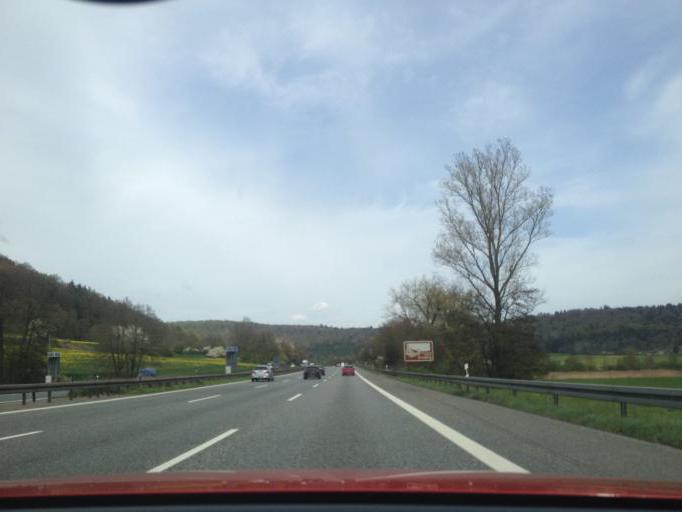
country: DE
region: Bavaria
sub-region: Regierungsbezirk Mittelfranken
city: Greding
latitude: 49.0158
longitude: 11.3596
